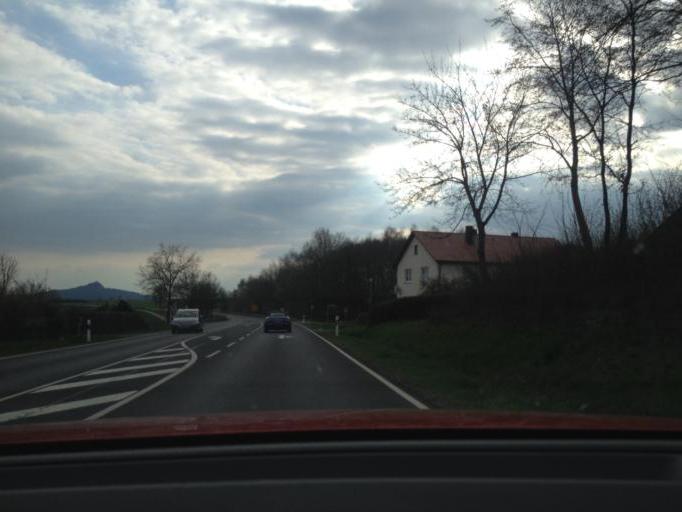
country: DE
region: Bavaria
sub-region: Upper Palatinate
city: Kulmain
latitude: 49.8867
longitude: 11.8905
